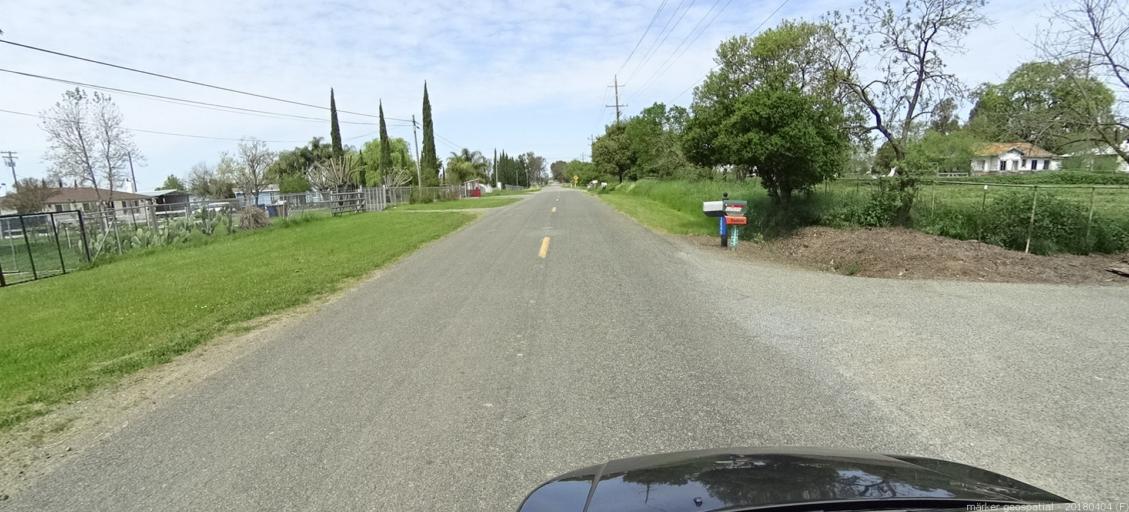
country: US
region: California
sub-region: Sacramento County
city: Herald
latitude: 38.2993
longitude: -121.2643
